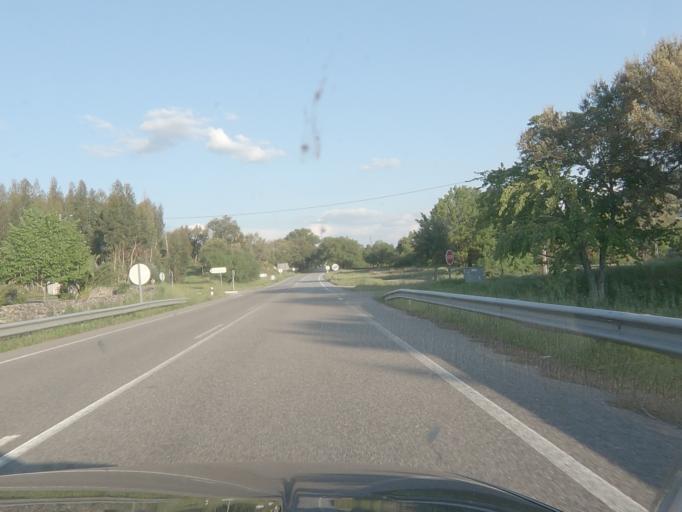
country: PT
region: Portalegre
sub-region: Portalegre
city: Sao Juliao
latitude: 39.3564
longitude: -7.3144
